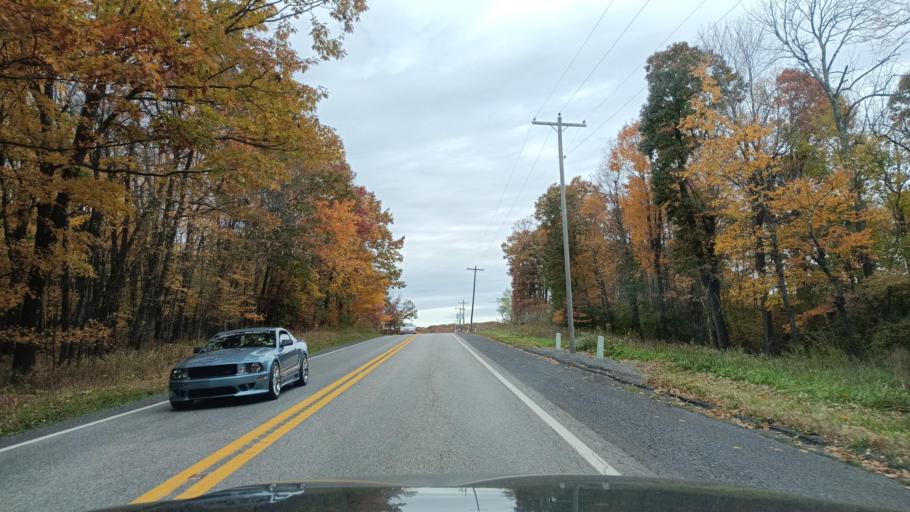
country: US
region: Maryland
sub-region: Garrett County
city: Mountain Lake Park
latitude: 39.2367
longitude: -79.2200
